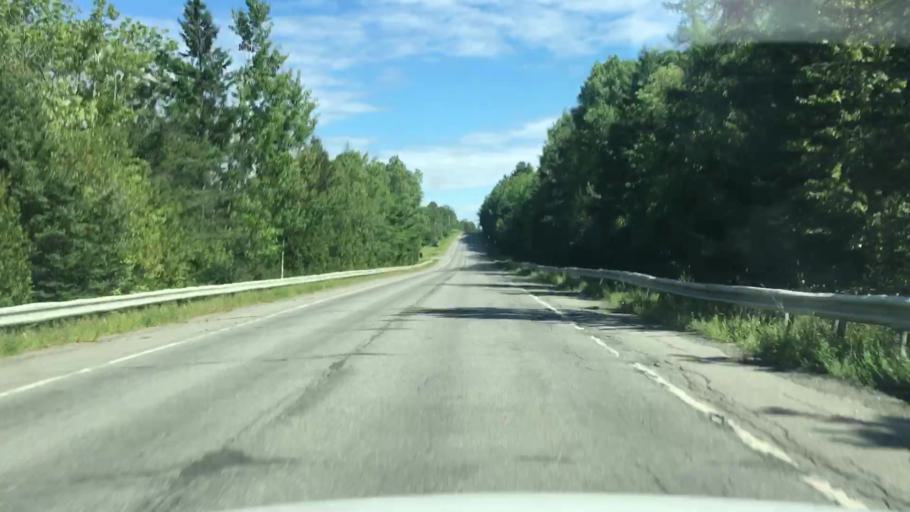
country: US
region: Maine
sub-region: Penobscot County
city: Dexter
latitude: 45.0554
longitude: -69.2563
